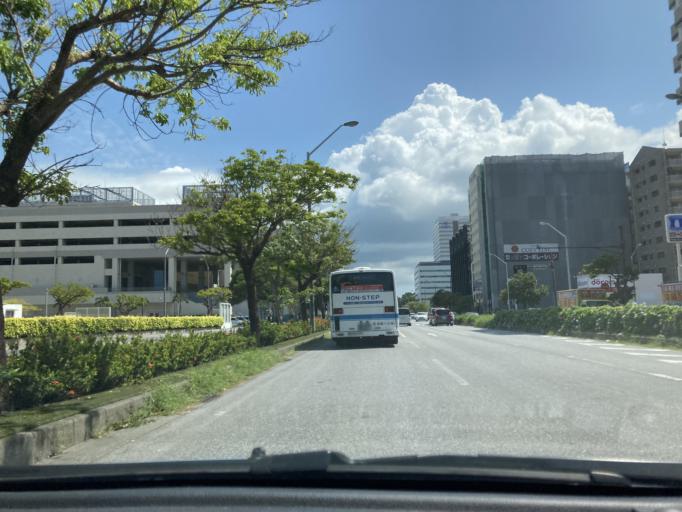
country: JP
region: Okinawa
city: Naha-shi
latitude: 26.2265
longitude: 127.6930
